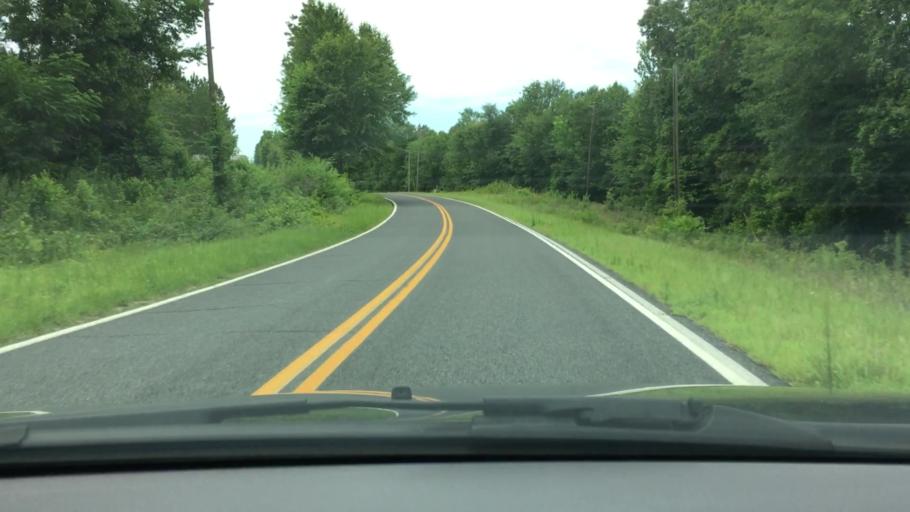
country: US
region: South Carolina
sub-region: Barnwell County
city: Williston
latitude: 33.6253
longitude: -81.3718
